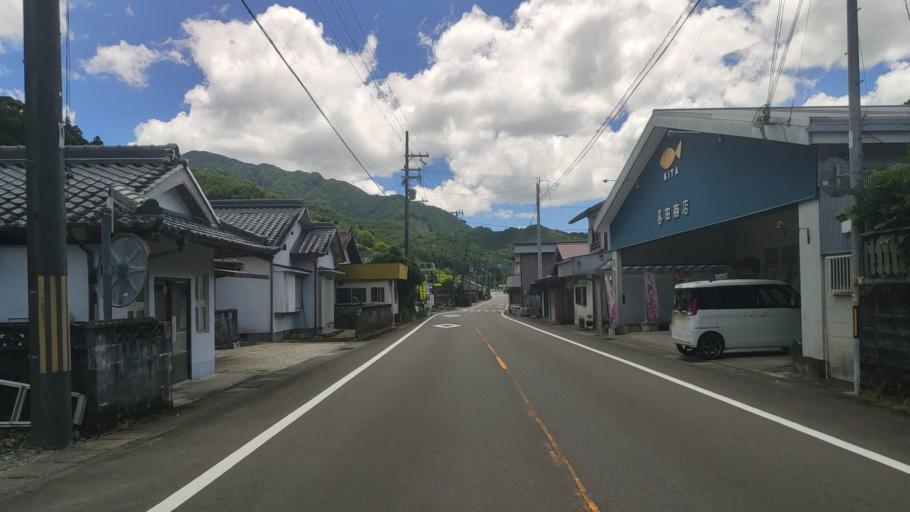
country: JP
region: Mie
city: Owase
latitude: 33.9775
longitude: 136.0532
